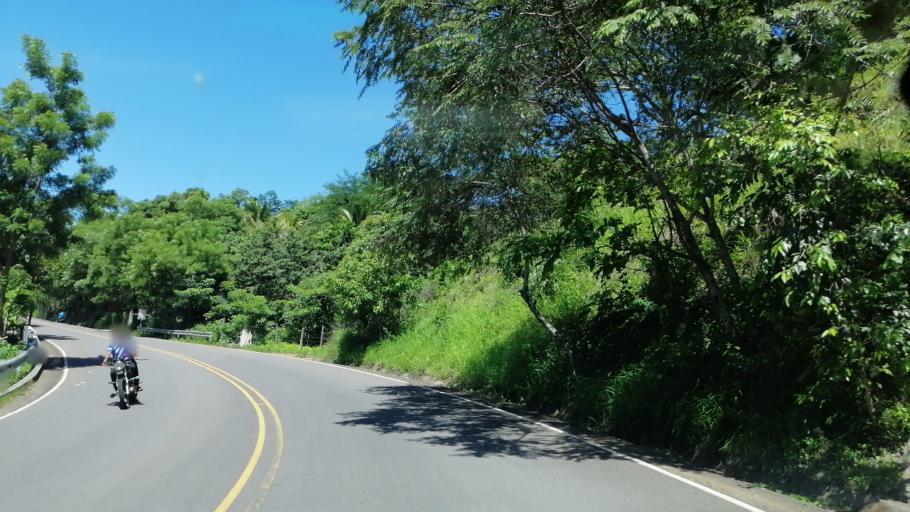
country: SV
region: San Miguel
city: Ciudad Barrios
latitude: 13.8124
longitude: -88.1831
